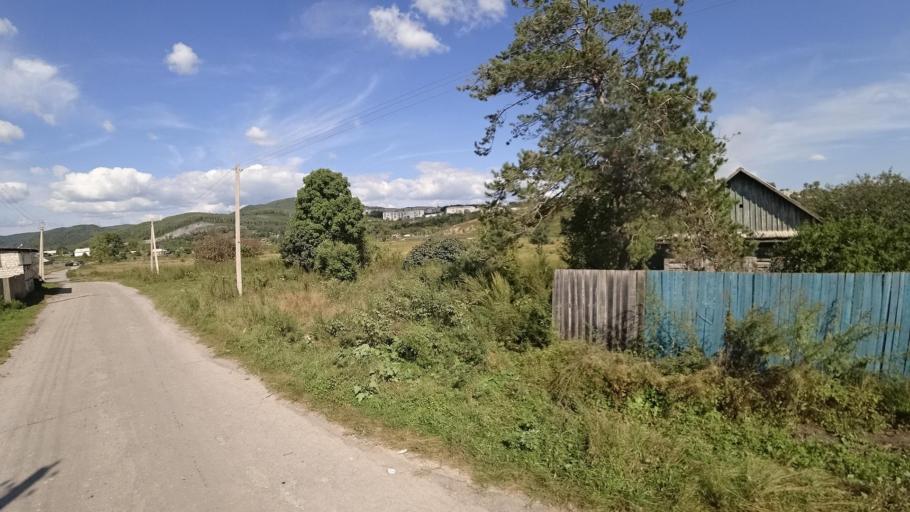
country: RU
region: Jewish Autonomous Oblast
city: Londoko
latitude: 49.0085
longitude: 131.8737
